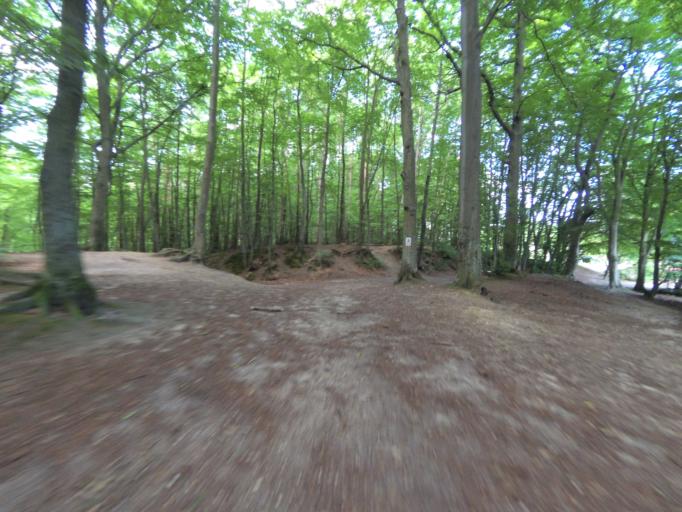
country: PL
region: Pomeranian Voivodeship
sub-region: Gdynia
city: Wielki Kack
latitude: 54.4920
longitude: 18.5060
